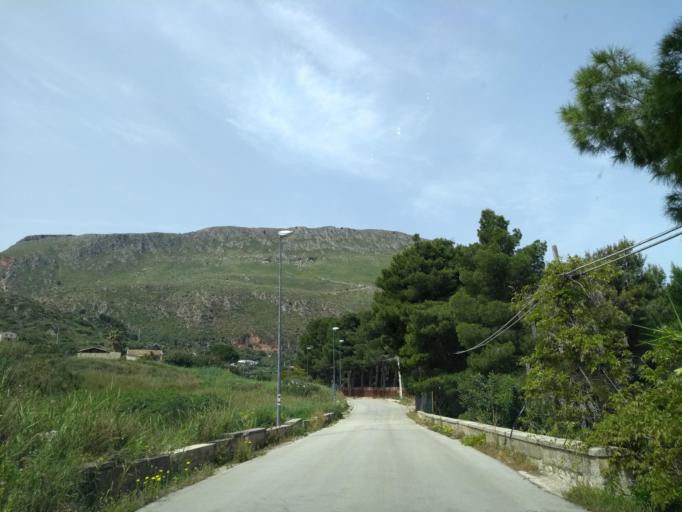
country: IT
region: Sicily
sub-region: Trapani
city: Castelluzzo
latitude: 38.0743
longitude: 12.8141
